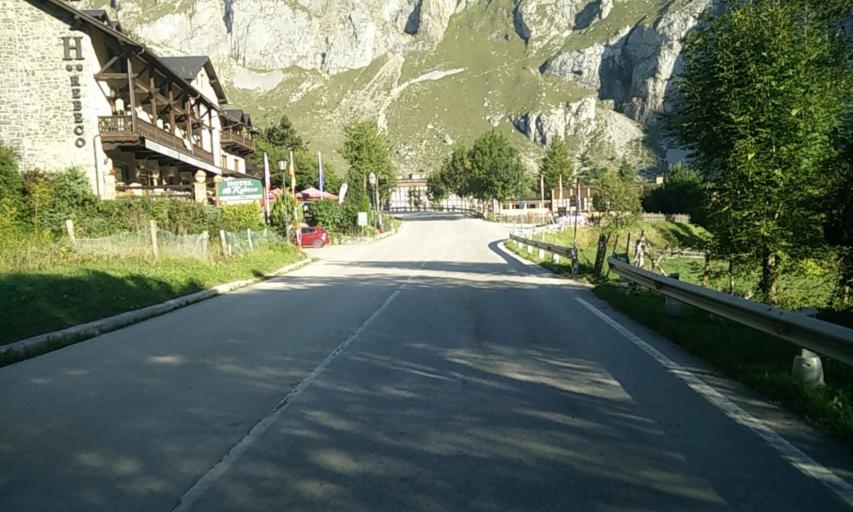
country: ES
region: Castille and Leon
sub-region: Provincia de Leon
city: Posada de Valdeon
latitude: 43.1432
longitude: -4.8103
